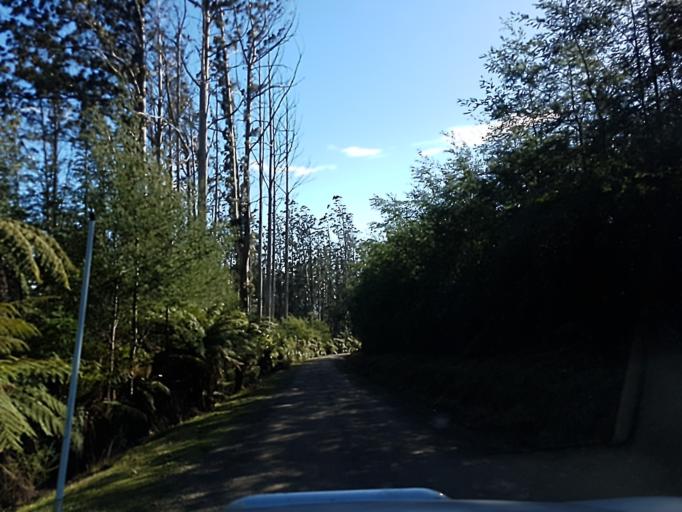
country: AU
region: Victoria
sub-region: Yarra Ranges
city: Healesville
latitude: -37.5700
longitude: 145.5164
